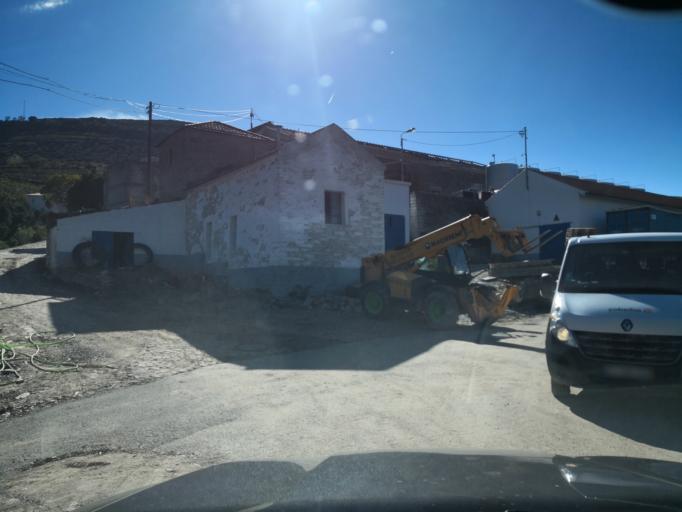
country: PT
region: Viseu
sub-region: Tabuaco
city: Tabuaco
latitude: 41.1775
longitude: -7.5146
